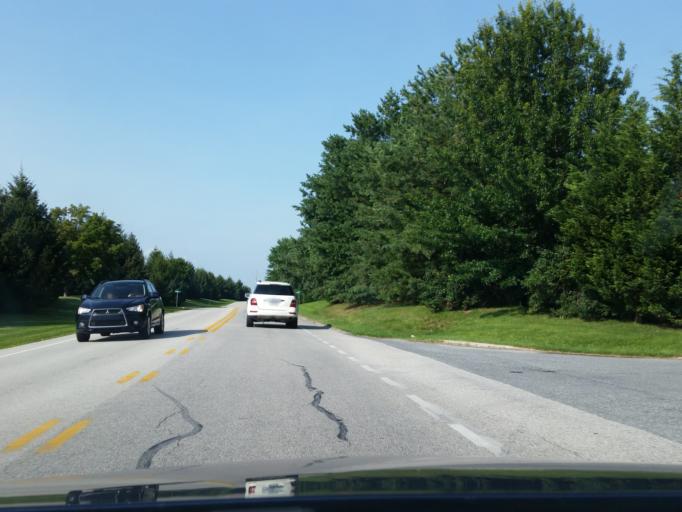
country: US
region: Pennsylvania
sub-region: York County
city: Shiloh
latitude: 39.9921
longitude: -76.7775
